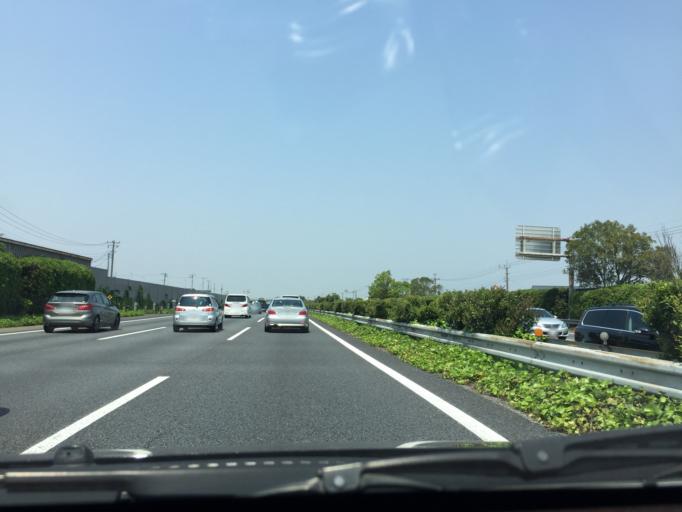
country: JP
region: Saitama
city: Kazo
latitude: 36.1315
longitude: 139.6225
